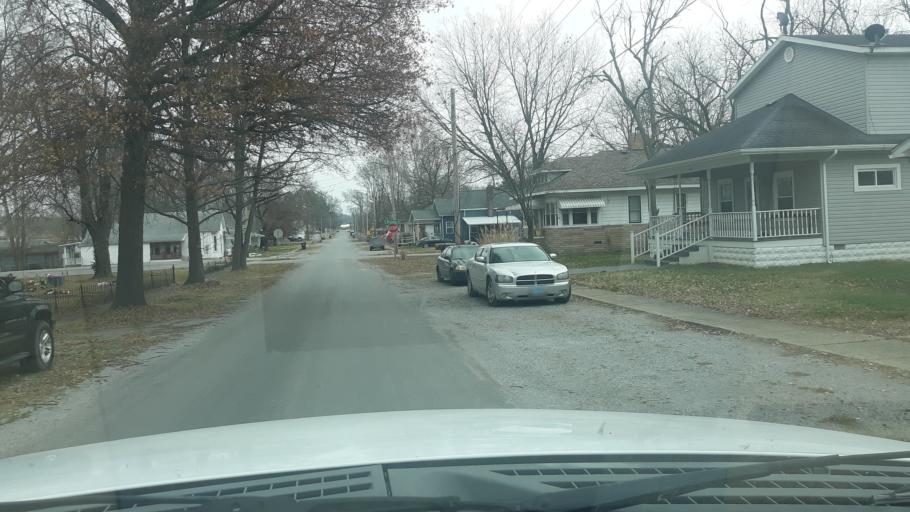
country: US
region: Illinois
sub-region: Saline County
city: Harrisburg
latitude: 37.8398
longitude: -88.6102
